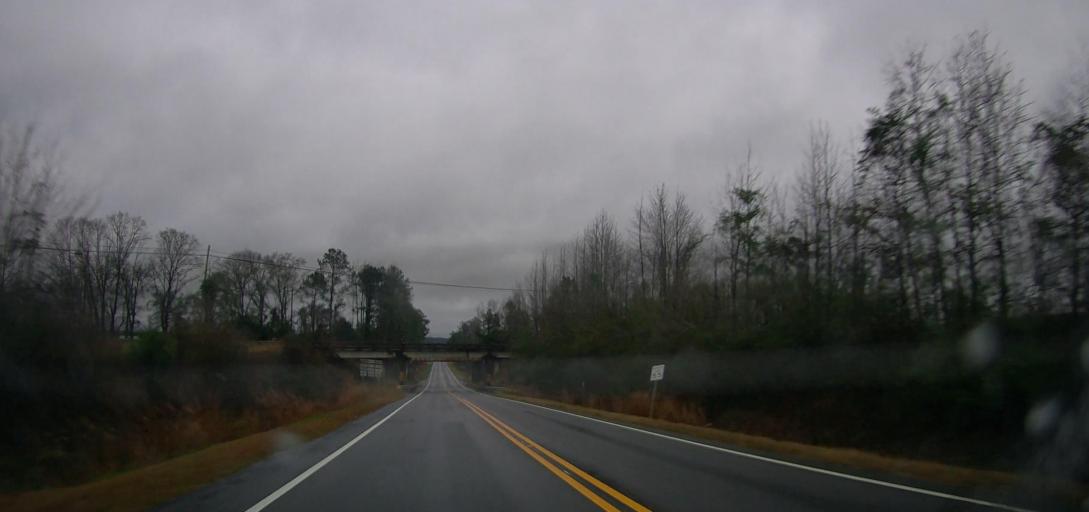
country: US
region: Alabama
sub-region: Chilton County
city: Thorsby
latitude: 32.7677
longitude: -86.8790
